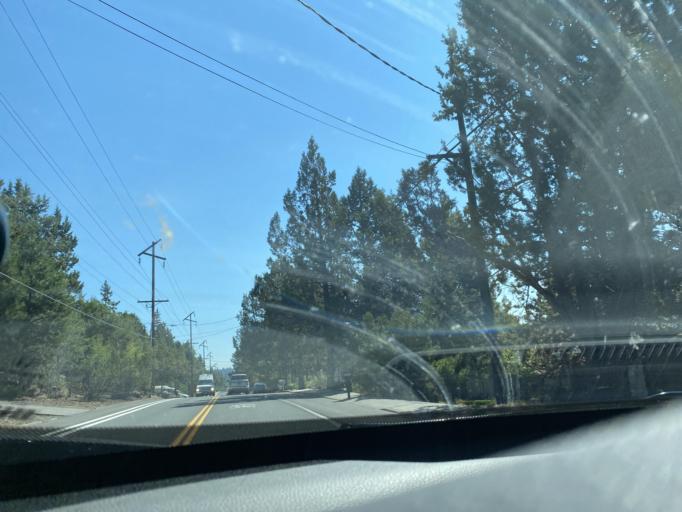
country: US
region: Oregon
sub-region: Deschutes County
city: Bend
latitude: 44.0641
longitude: -121.3334
